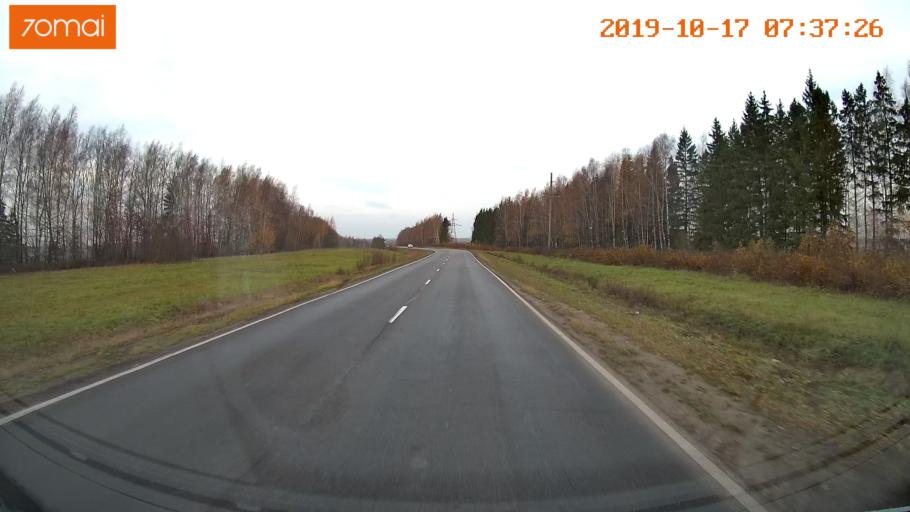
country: RU
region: Vladimir
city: Yur'yev-Pol'skiy
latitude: 56.4493
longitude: 39.8992
